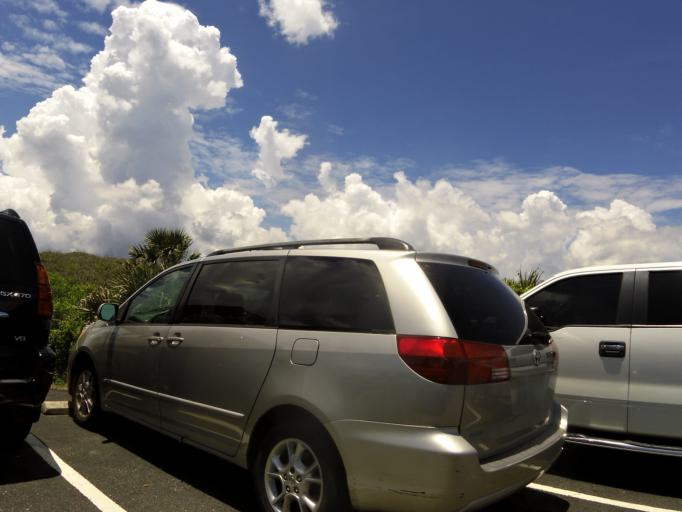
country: US
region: Florida
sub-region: Saint Johns County
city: Palm Valley
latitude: 30.1166
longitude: -81.3462
